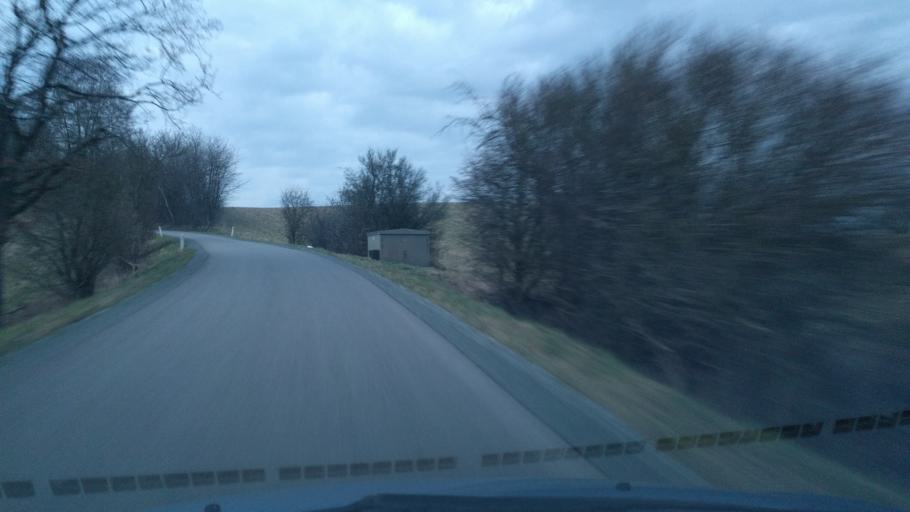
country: DK
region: South Denmark
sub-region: Haderslev Kommune
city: Haderslev
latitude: 55.2583
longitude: 9.4272
